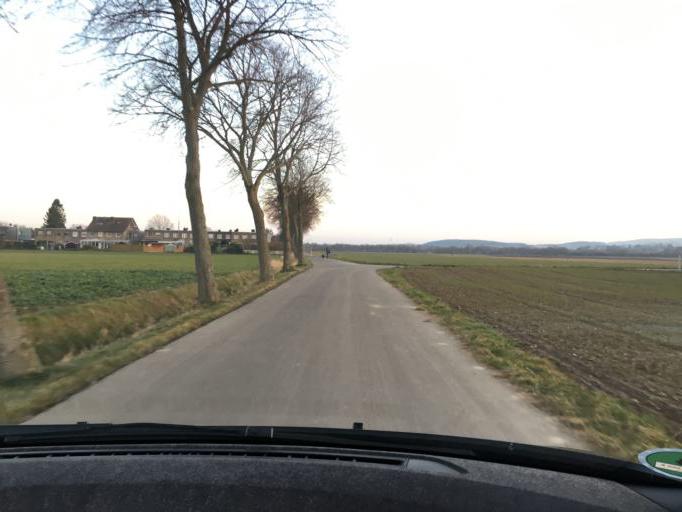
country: DE
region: North Rhine-Westphalia
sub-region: Regierungsbezirk Koln
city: Dueren
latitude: 50.7789
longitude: 6.4625
